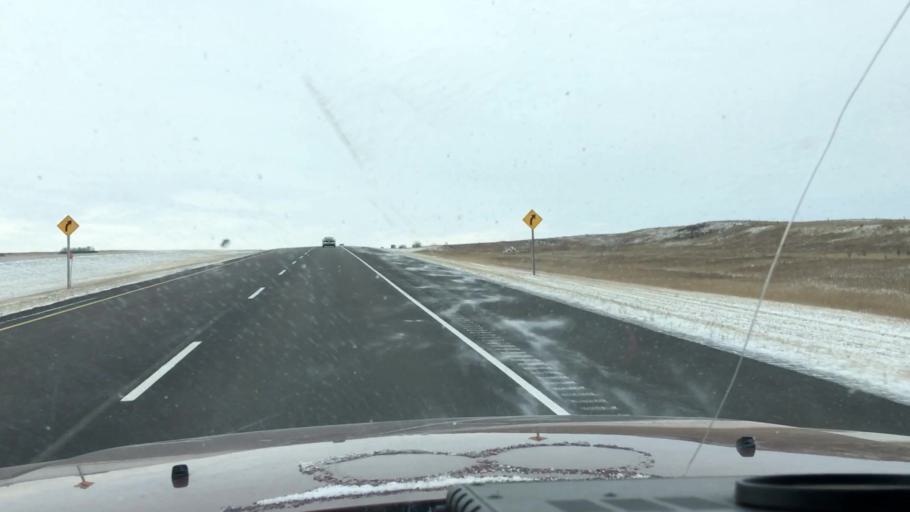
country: CA
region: Saskatchewan
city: Saskatoon
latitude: 51.7230
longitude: -106.4714
